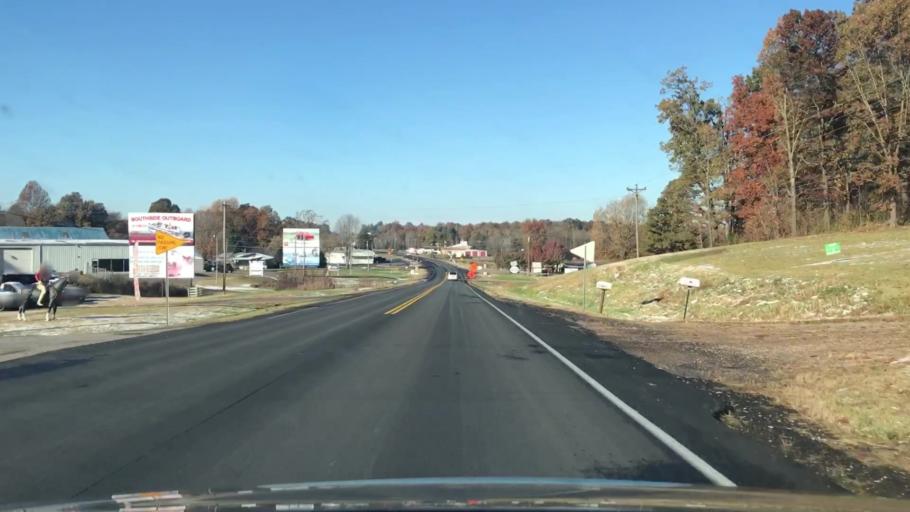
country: US
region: Kentucky
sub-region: Livingston County
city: Ledbetter
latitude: 37.0061
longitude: -88.4267
